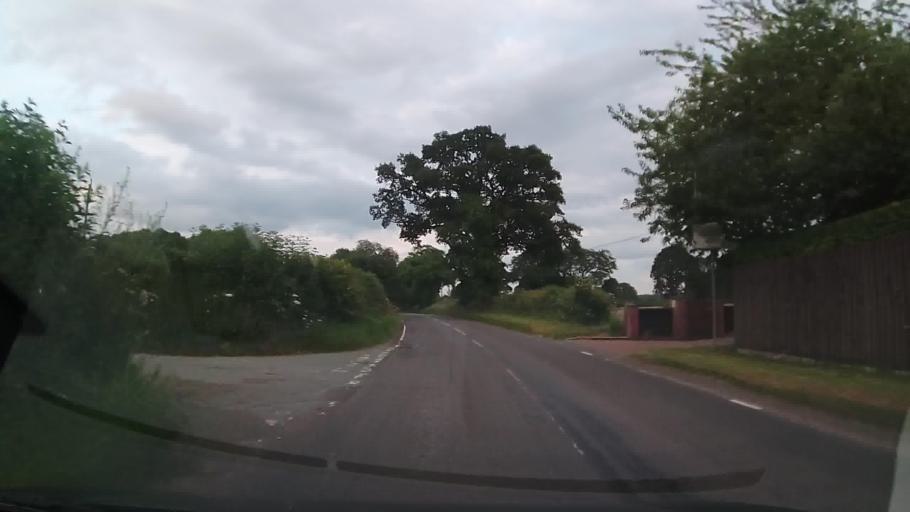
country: GB
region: England
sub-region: Shropshire
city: Great Ness
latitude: 52.7978
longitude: -2.9305
